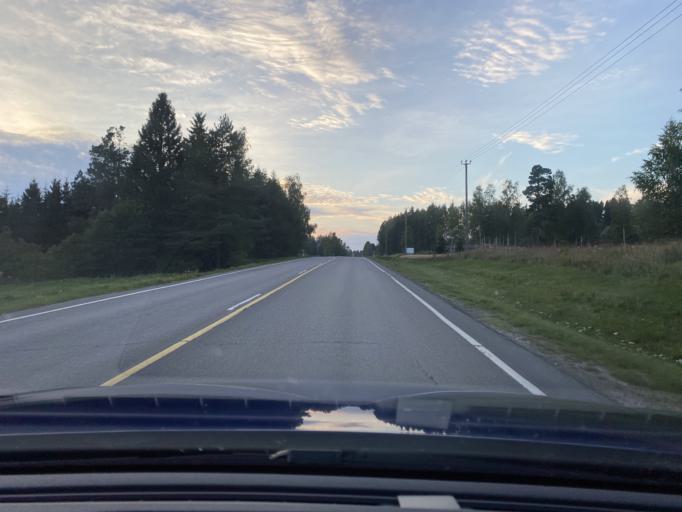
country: FI
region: Satakunta
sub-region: Pohjois-Satakunta
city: Kankaanpaeae
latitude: 61.7885
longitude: 22.4162
